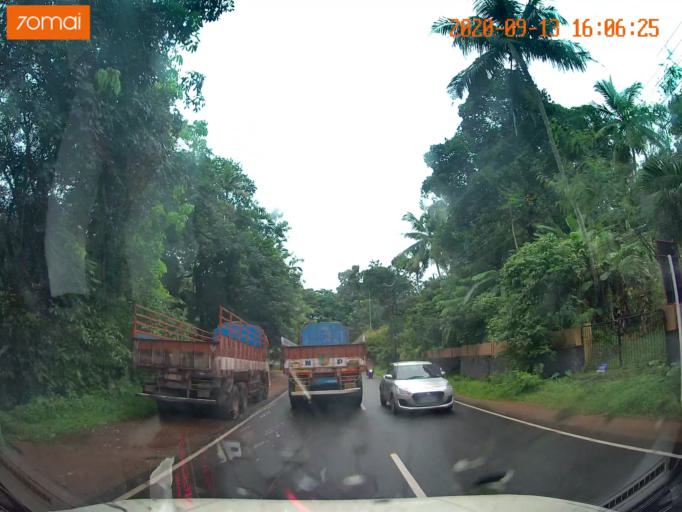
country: IN
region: Kerala
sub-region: Kottayam
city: Palackattumala
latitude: 9.6708
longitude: 76.5813
